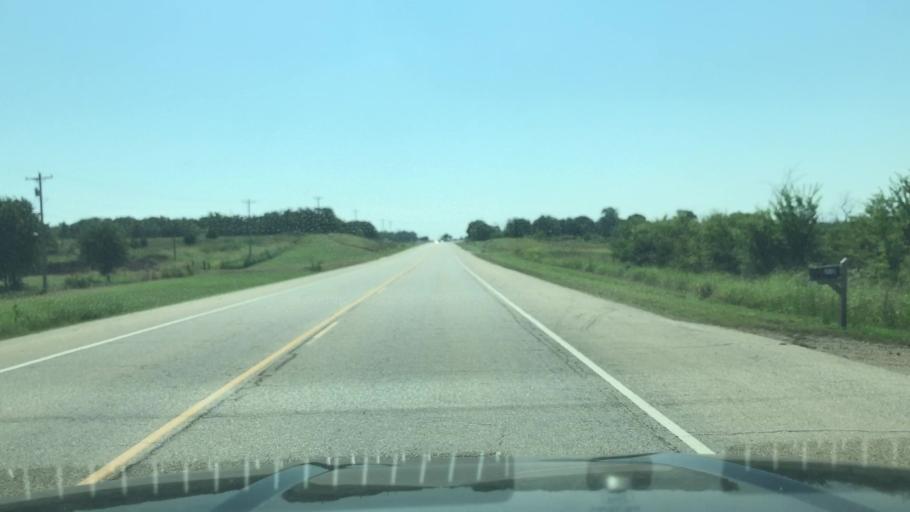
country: US
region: Oklahoma
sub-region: Creek County
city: Mannford
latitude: 36.0018
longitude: -96.3741
